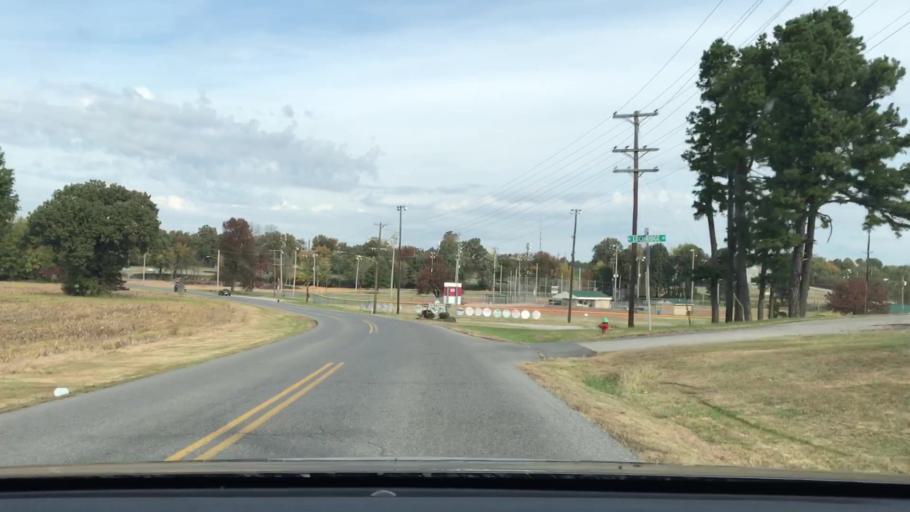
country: US
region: Kentucky
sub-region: Graves County
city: Mayfield
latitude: 36.7483
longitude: -88.6495
